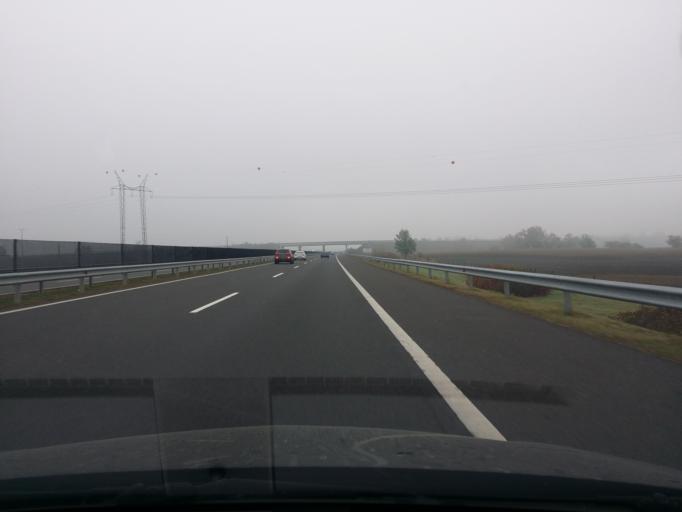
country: HU
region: Hajdu-Bihar
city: Hajdunanas
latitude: 47.8596
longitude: 21.3603
